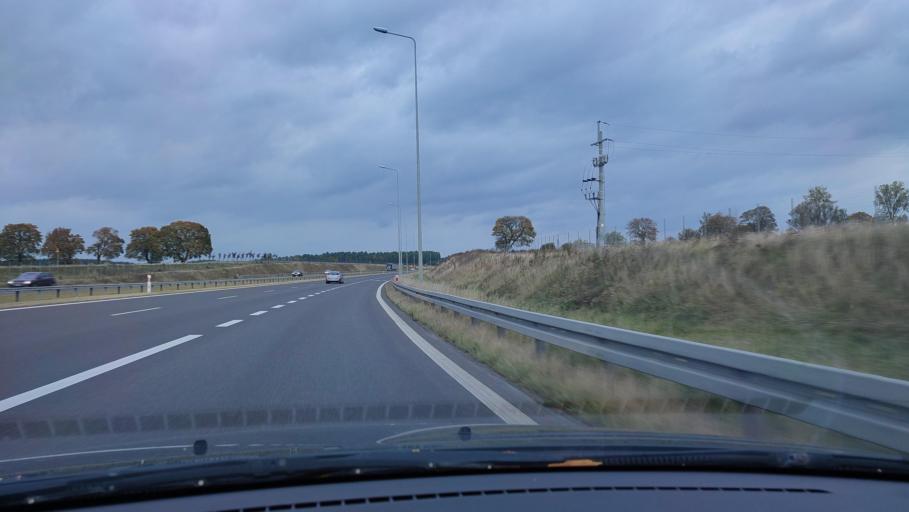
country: PL
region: Masovian Voivodeship
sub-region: Powiat mlawski
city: Wieczfnia Koscielna
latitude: 53.2305
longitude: 20.4195
